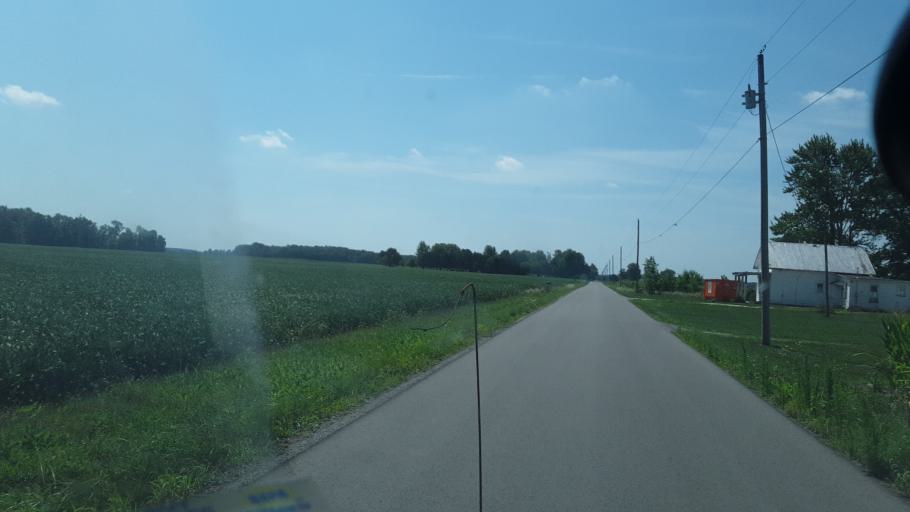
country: US
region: Ohio
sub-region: Hancock County
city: Findlay
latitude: 41.0052
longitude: -83.5160
